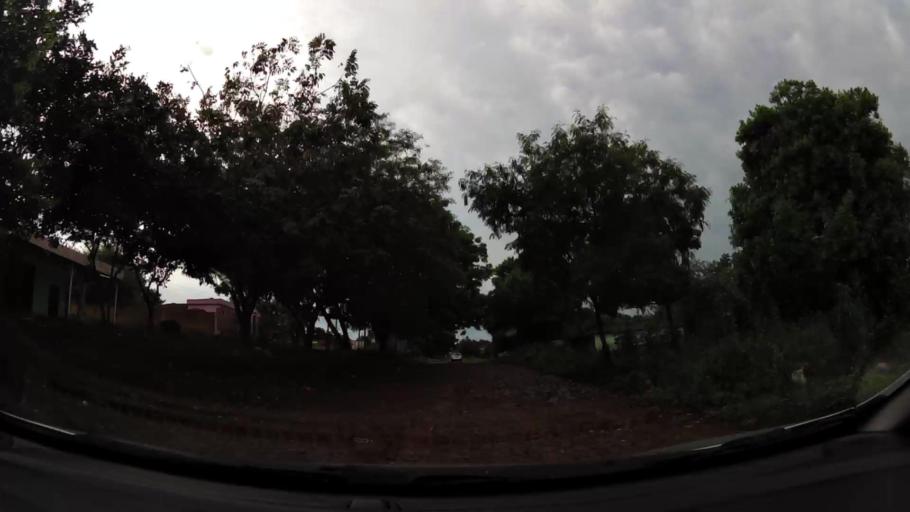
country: PY
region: Alto Parana
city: Presidente Franco
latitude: -25.5292
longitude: -54.6678
